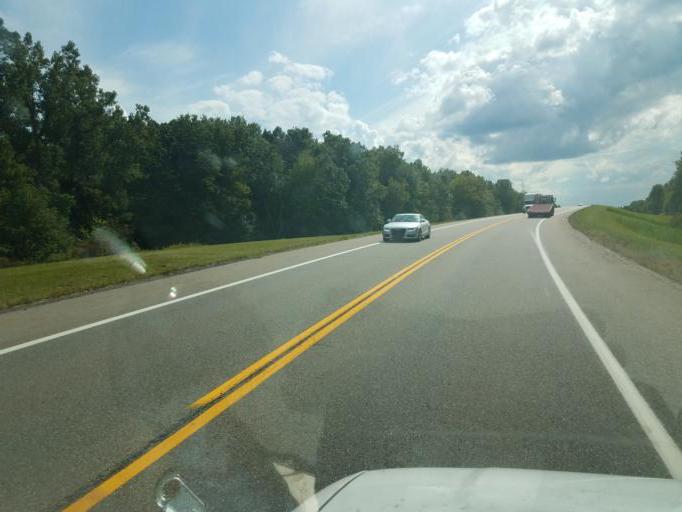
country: US
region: Ohio
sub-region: Portage County
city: Ravenna
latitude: 41.1292
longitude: -81.2308
